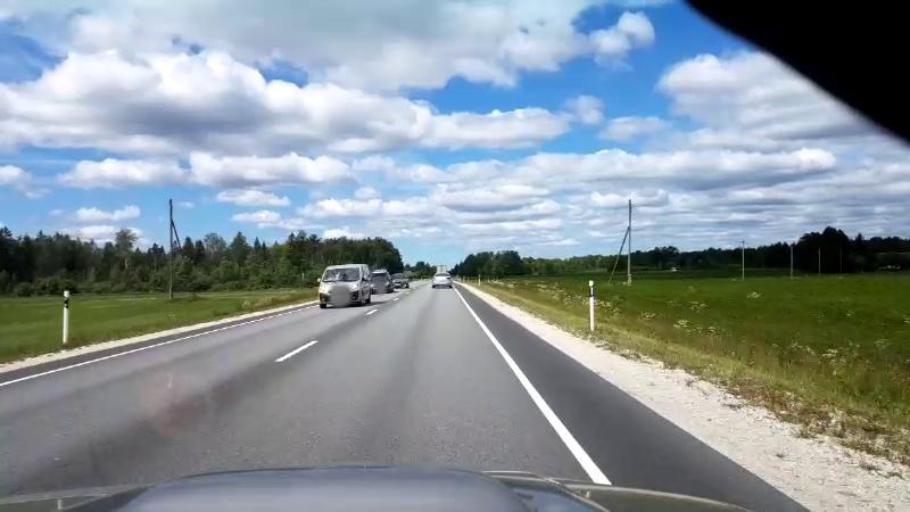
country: EE
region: Paernumaa
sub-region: Halinga vald
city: Parnu-Jaagupi
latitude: 58.6472
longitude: 24.4838
